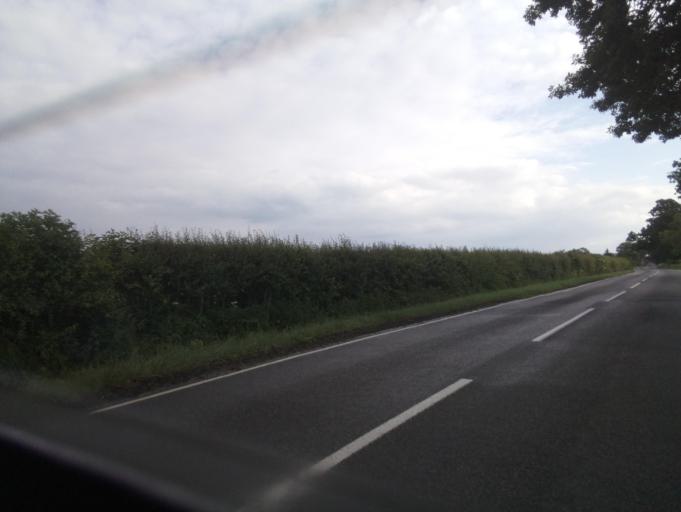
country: GB
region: England
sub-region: Lincolnshire
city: Great Gonerby
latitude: 53.0367
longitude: -0.6496
